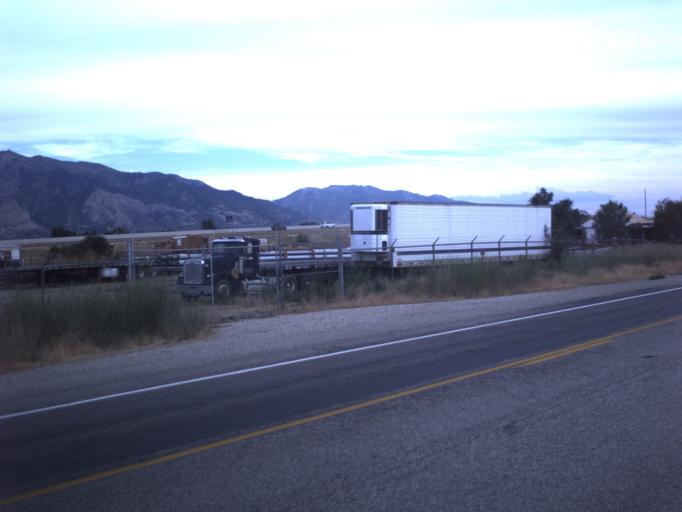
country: US
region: Utah
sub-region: Weber County
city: Marriott-Slaterville
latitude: 41.2720
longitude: -112.0282
